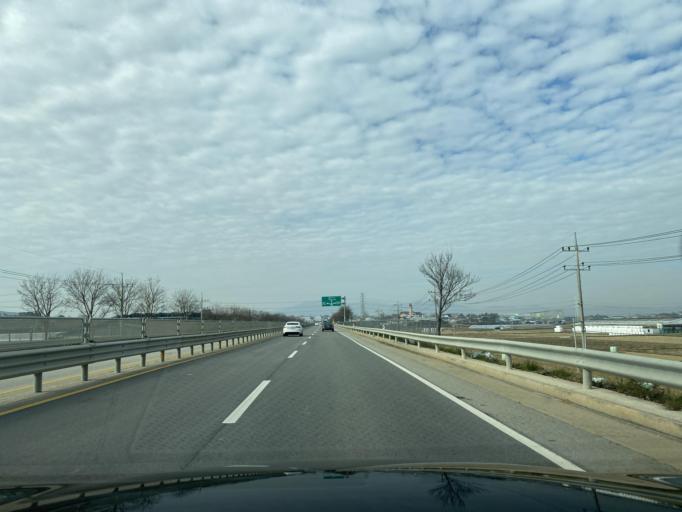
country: KR
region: Chungcheongnam-do
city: Yesan
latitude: 36.6867
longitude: 126.7668
